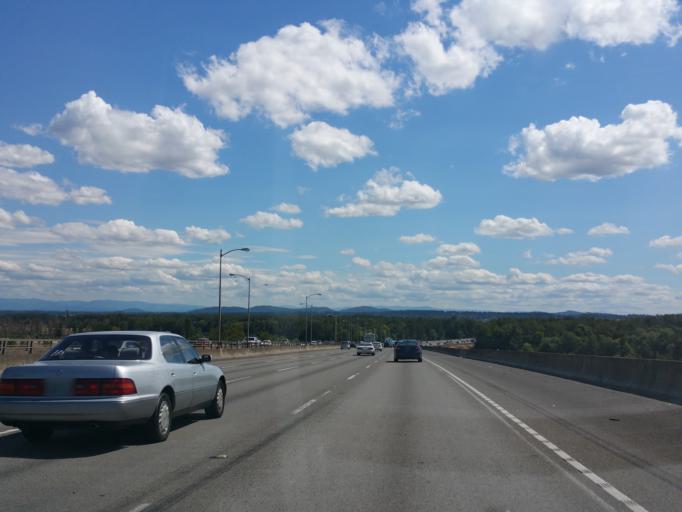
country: US
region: Washington
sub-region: Clark County
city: Mill Plain
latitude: 45.5921
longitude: -122.5483
